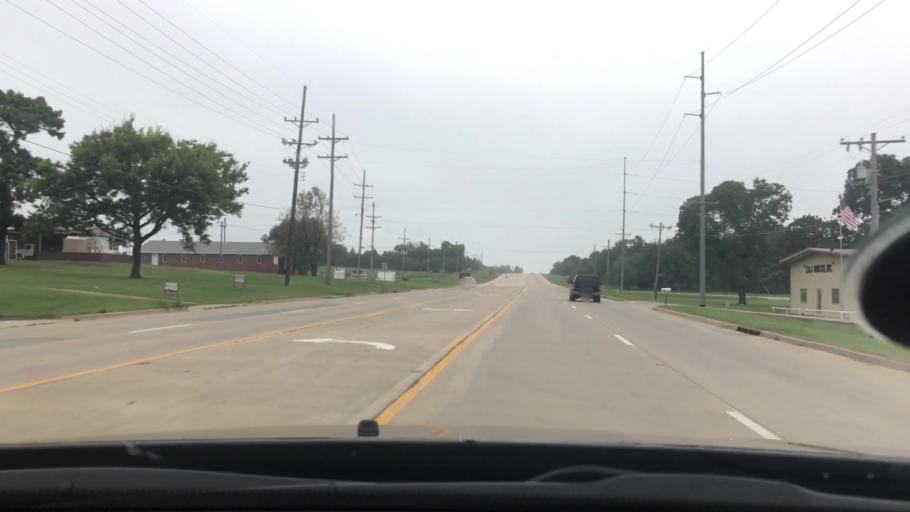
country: US
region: Oklahoma
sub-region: Seminole County
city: Seminole
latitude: 35.2594
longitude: -96.6710
